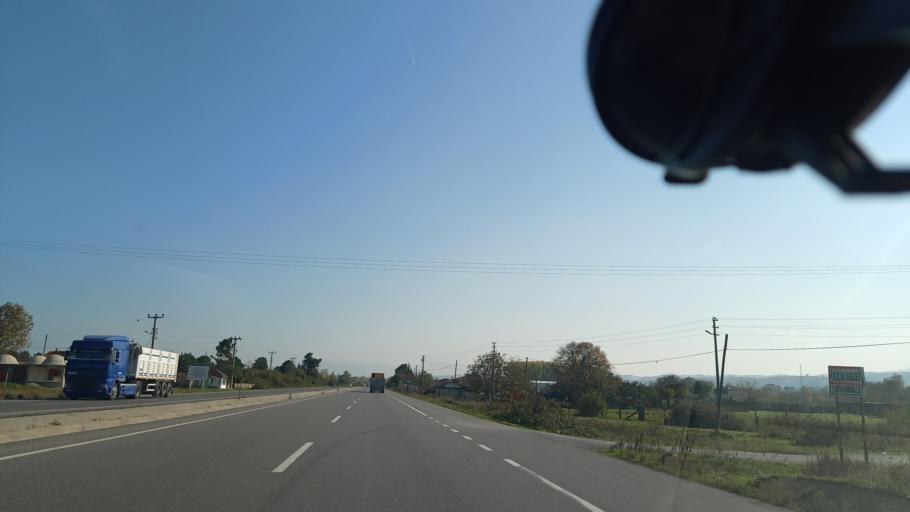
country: TR
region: Sakarya
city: Karasu
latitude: 41.0798
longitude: 30.7710
